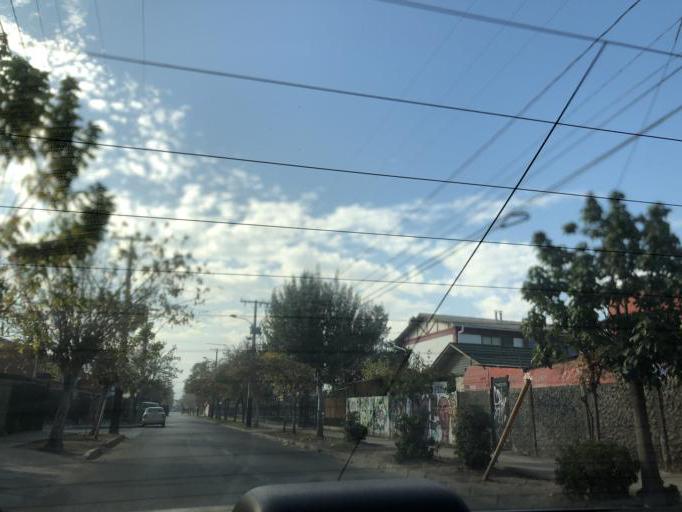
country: CL
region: Santiago Metropolitan
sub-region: Provincia de Cordillera
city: Puente Alto
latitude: -33.5909
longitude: -70.5647
